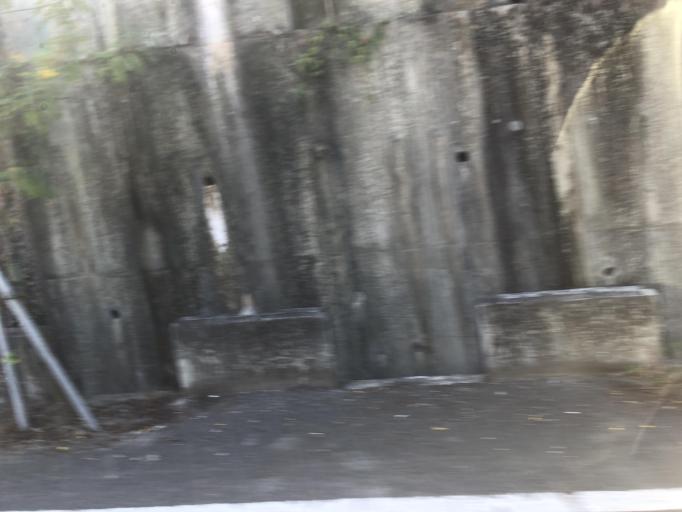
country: TW
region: Taiwan
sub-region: Tainan
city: Tainan
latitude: 23.0358
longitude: 120.3428
